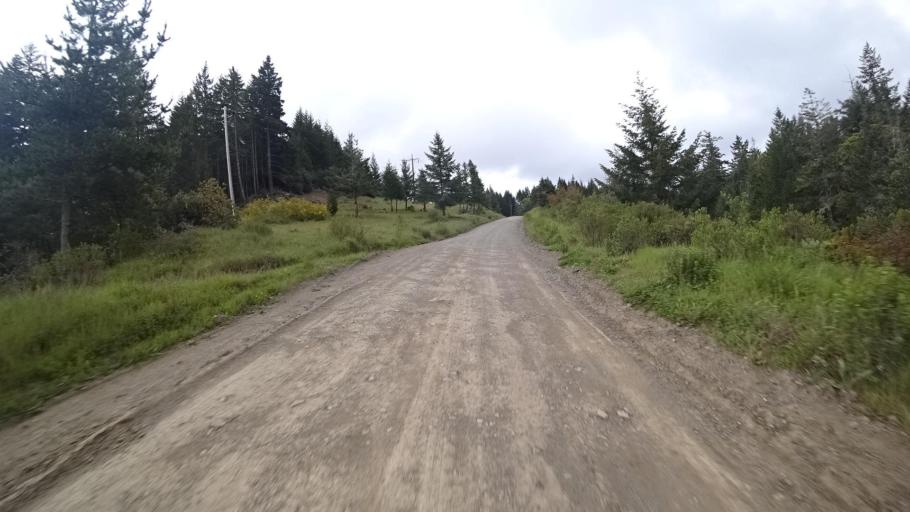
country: US
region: California
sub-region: Humboldt County
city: Redway
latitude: 40.2403
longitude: -123.7627
